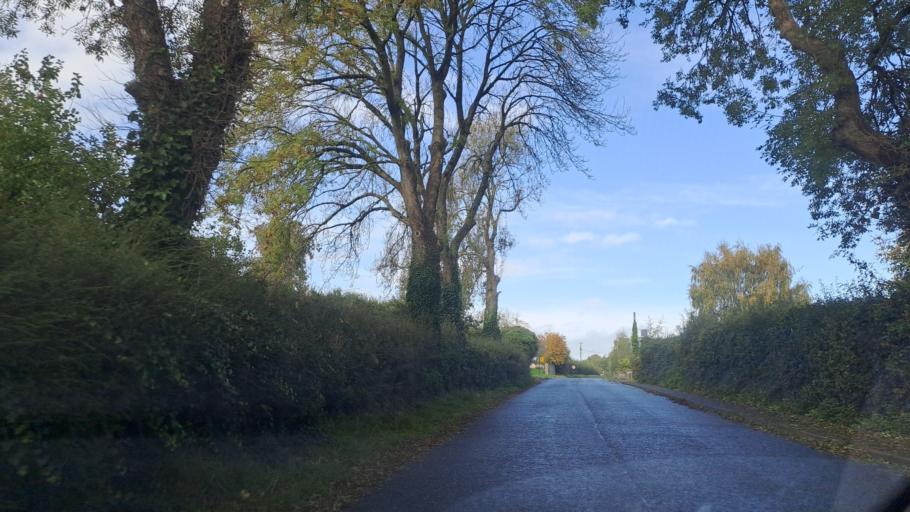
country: IE
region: Leinster
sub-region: Lu
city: Ardee
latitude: 53.8529
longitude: -6.6578
